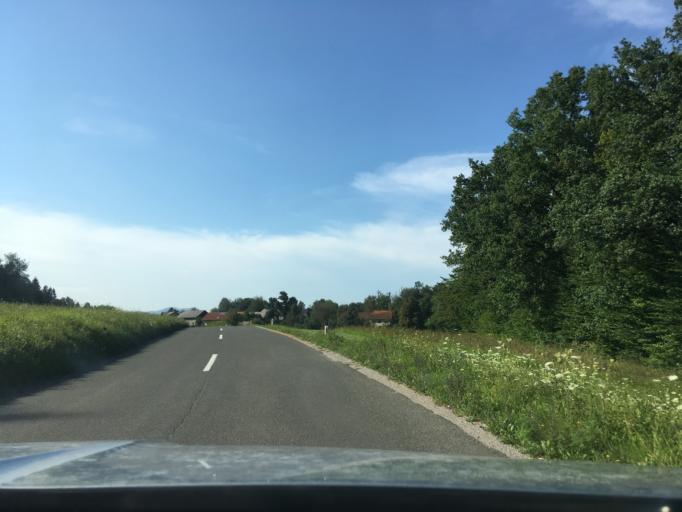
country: SI
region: Crnomelj
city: Crnomelj
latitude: 45.5050
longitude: 15.1899
